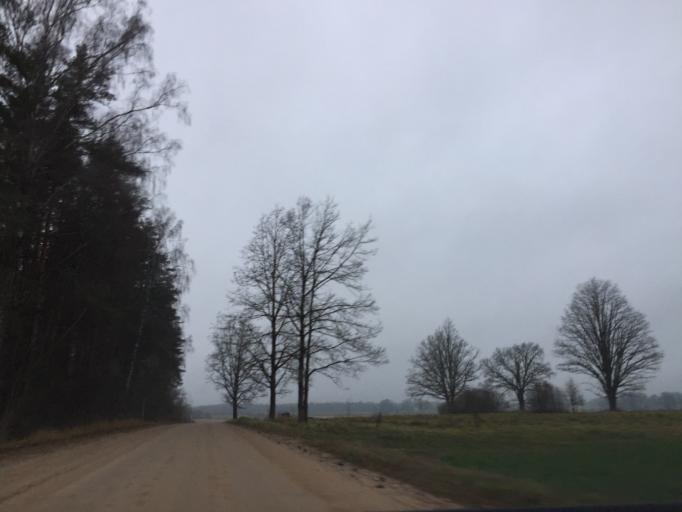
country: LV
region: Koceni
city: Koceni
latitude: 57.5429
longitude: 25.3295
